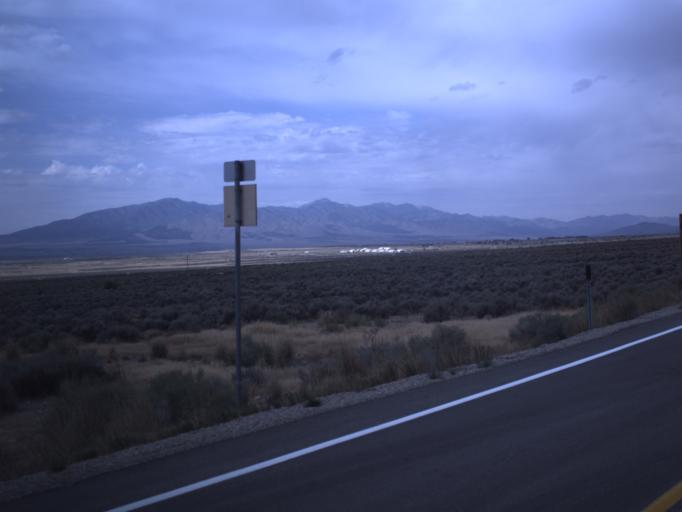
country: US
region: Utah
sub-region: Tooele County
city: Tooele
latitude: 40.2979
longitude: -112.2751
